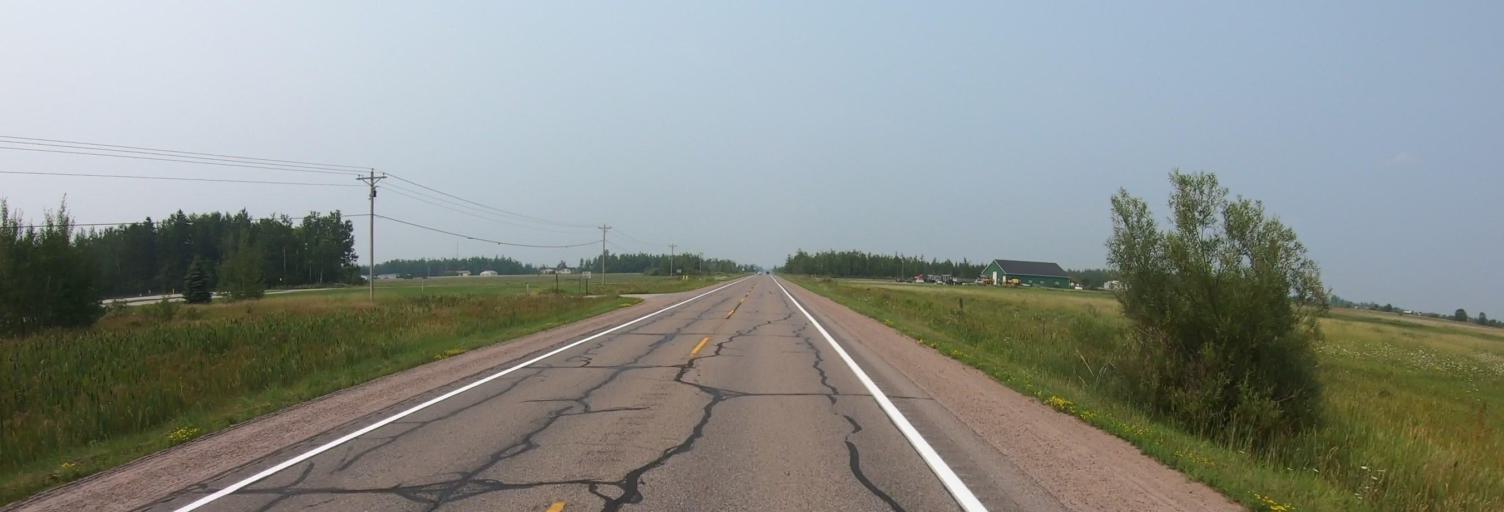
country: US
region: Michigan
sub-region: Chippewa County
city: Sault Ste. Marie
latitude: 46.4218
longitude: -84.3534
